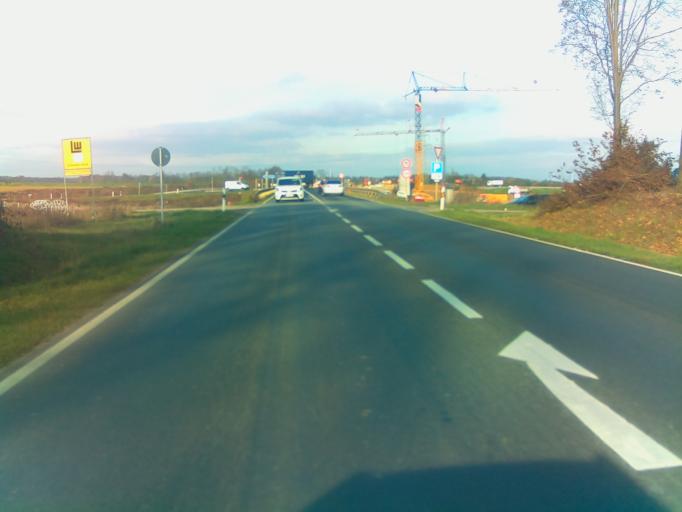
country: DE
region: Bavaria
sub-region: Regierungsbezirk Unterfranken
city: Esselbach
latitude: 49.8154
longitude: 9.5571
